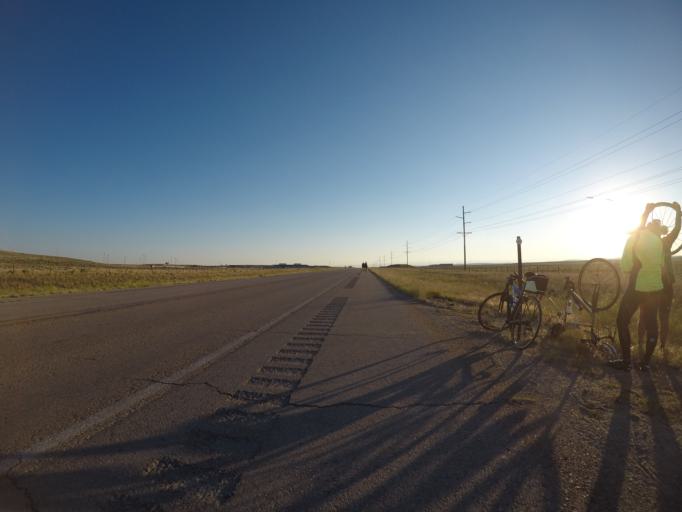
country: US
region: Wyoming
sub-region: Sublette County
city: Marbleton
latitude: 42.5770
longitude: -110.0925
